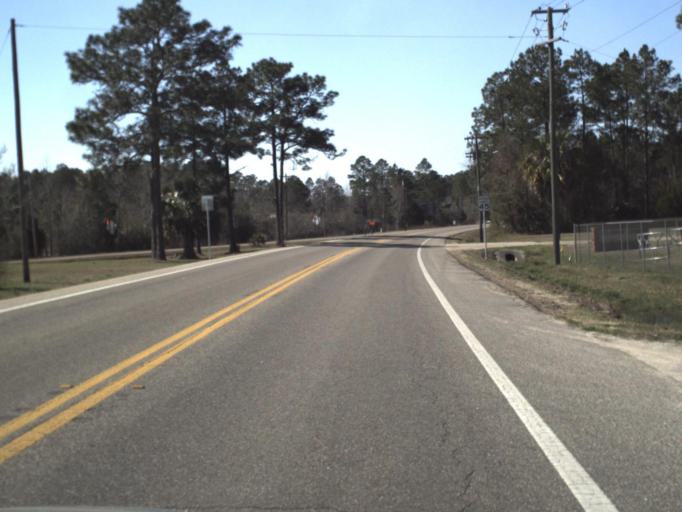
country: US
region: Florida
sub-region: Calhoun County
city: Blountstown
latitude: 30.4529
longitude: -85.0573
